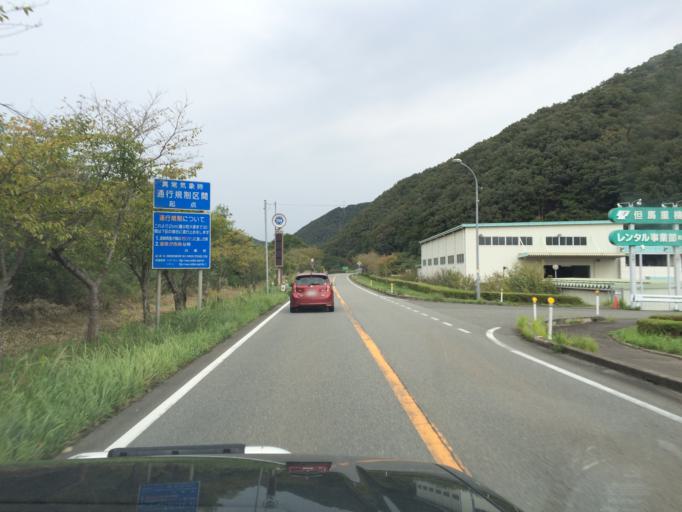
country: JP
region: Hyogo
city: Toyooka
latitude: 35.3597
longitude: 134.8294
